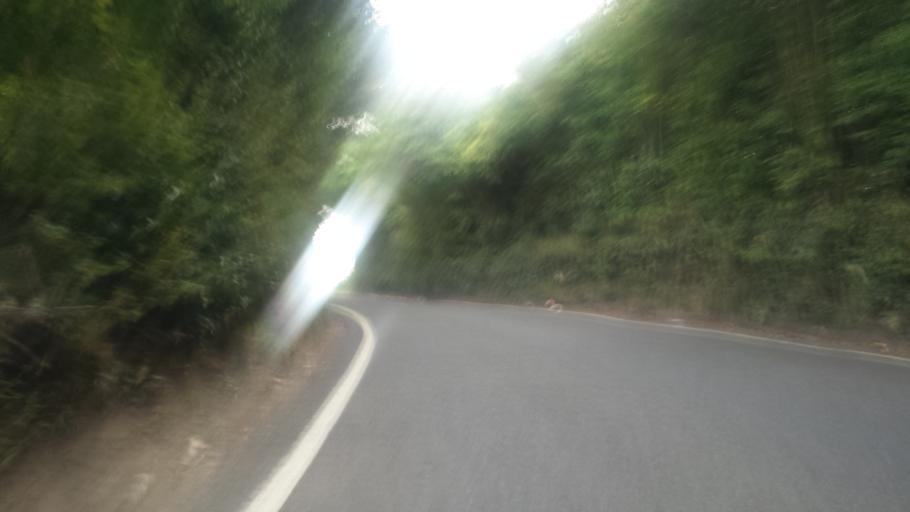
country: GB
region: England
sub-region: Kent
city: Swanley
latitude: 51.3861
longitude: 0.1870
